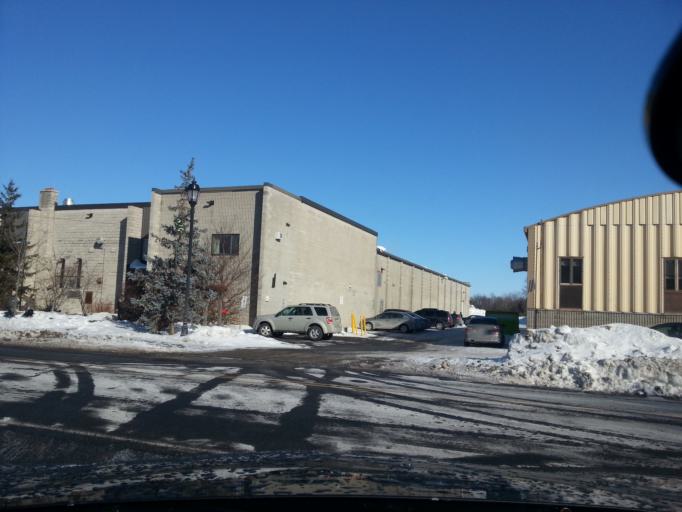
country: CA
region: Ontario
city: Ottawa
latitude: 45.2294
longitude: -75.4695
